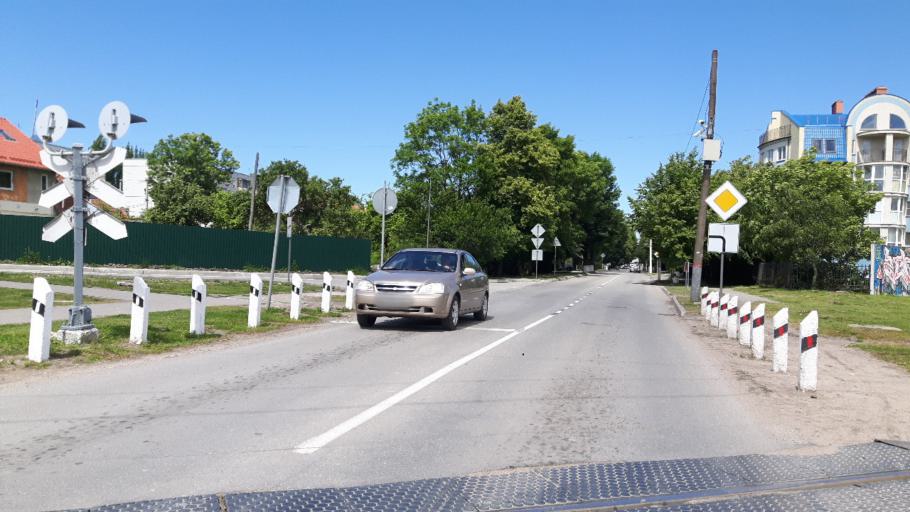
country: RU
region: Kaliningrad
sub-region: Zelenogradskiy Rayon
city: Zelenogradsk
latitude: 54.9531
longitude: 20.4707
